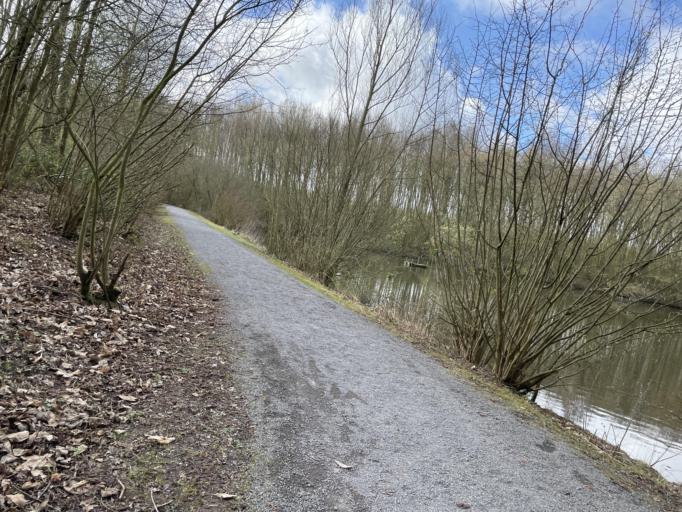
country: NL
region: South Holland
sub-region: Gemeente Pijnacker-Nootdorp
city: Pijnacker
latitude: 52.0474
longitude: 4.4554
